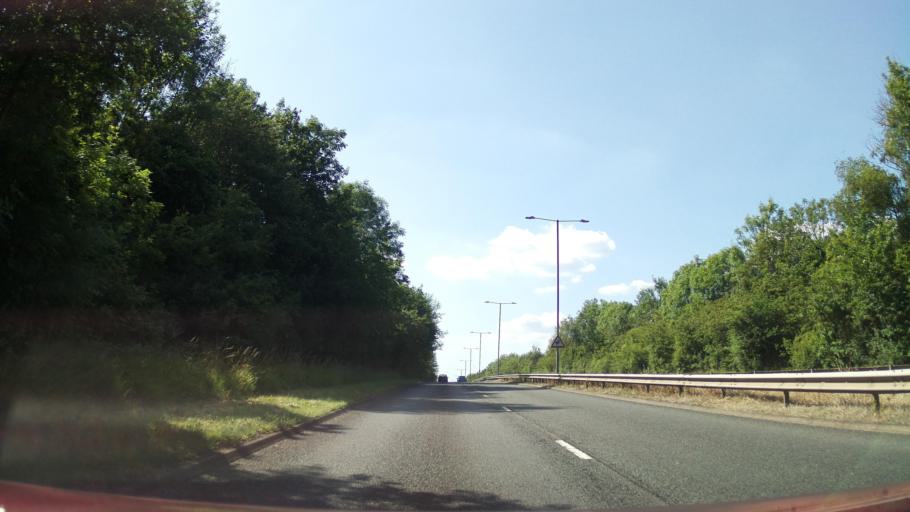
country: GB
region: England
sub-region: Worcestershire
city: Redditch
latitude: 52.2950
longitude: -1.9461
